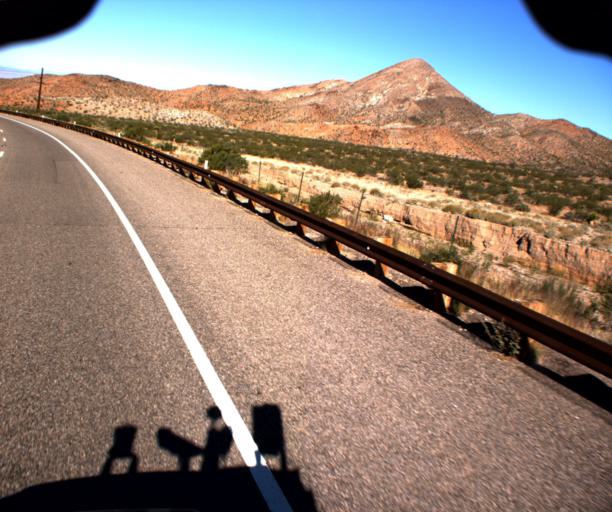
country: US
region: Nevada
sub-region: Clark County
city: Laughlin
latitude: 35.1998
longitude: -114.4237
